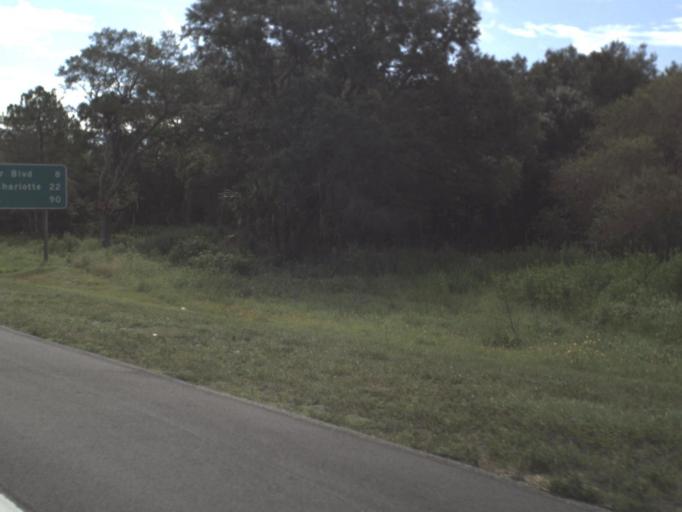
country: US
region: Florida
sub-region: Sarasota County
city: Plantation
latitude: 27.1116
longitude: -82.3335
